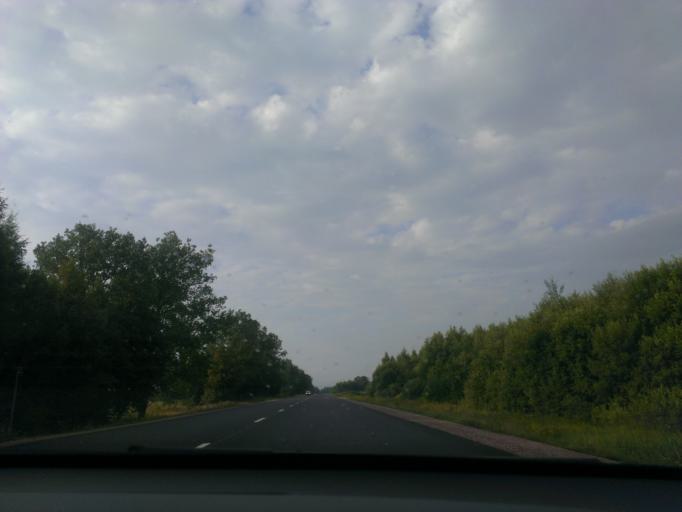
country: LV
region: Lecava
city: Iecava
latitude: 56.6742
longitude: 24.2362
